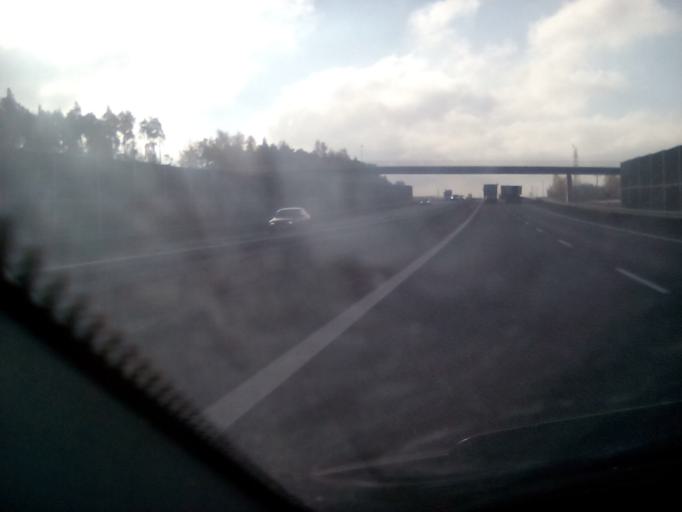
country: PL
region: Masovian Voivodeship
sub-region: Powiat bialobrzeski
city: Promna
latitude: 51.7248
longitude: 20.9193
